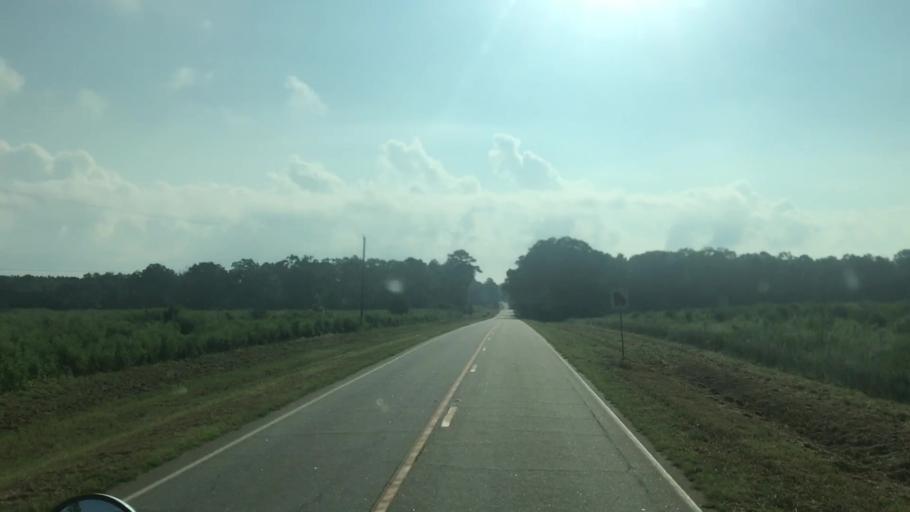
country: US
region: Florida
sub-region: Gadsden County
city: Quincy
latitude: 30.6985
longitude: -84.5324
